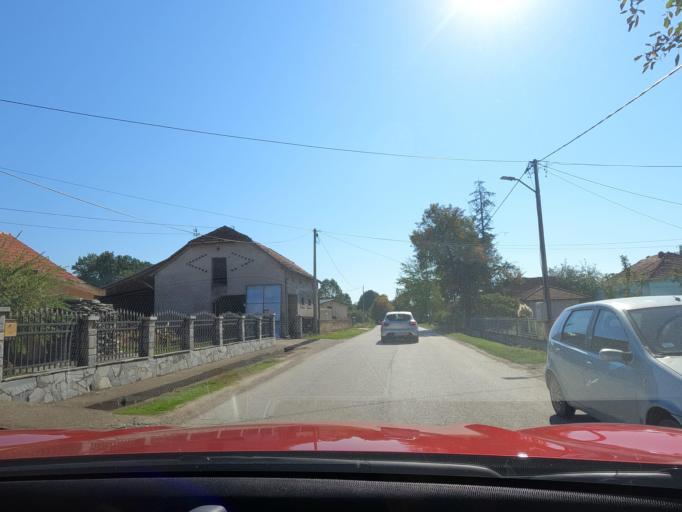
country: RS
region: Central Serbia
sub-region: Raski Okrug
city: Kraljevo
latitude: 43.7654
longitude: 20.6719
